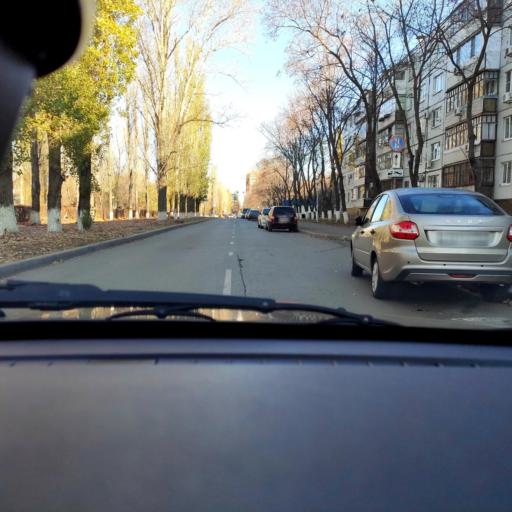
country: RU
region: Samara
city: Tol'yatti
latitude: 53.5204
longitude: 49.2850
